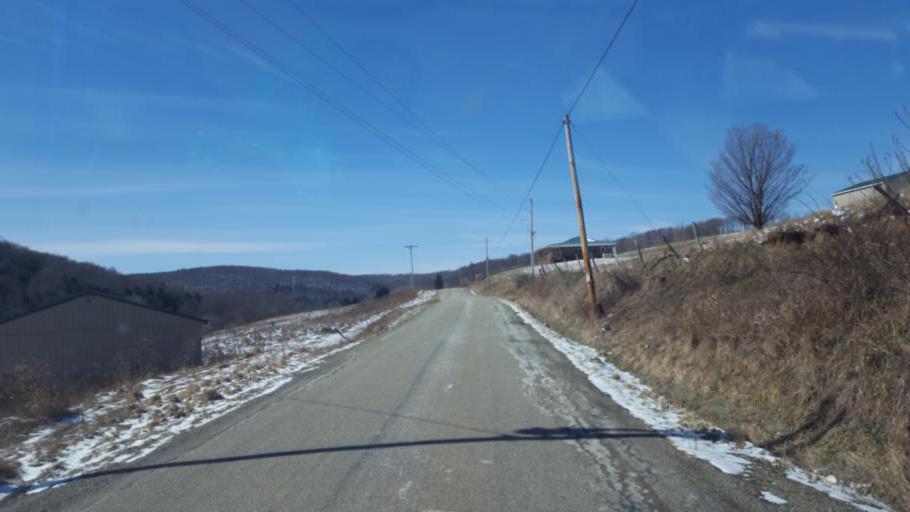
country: US
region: New York
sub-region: Allegany County
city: Andover
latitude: 41.9494
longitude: -77.7985
